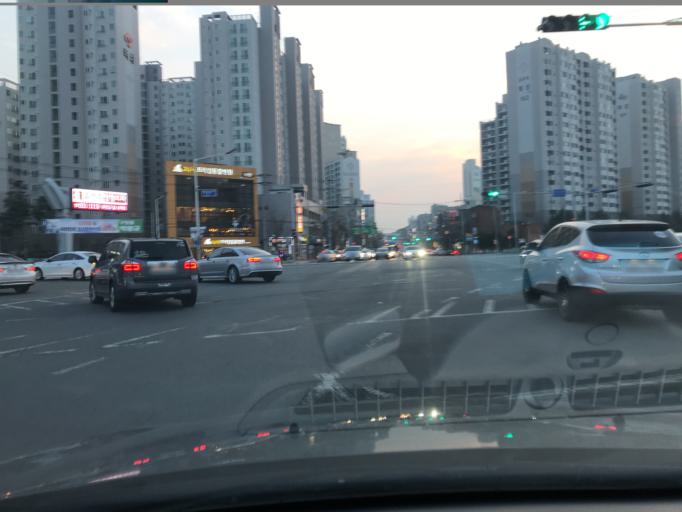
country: KR
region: Daegu
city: Hwawon
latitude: 35.8109
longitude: 128.5160
